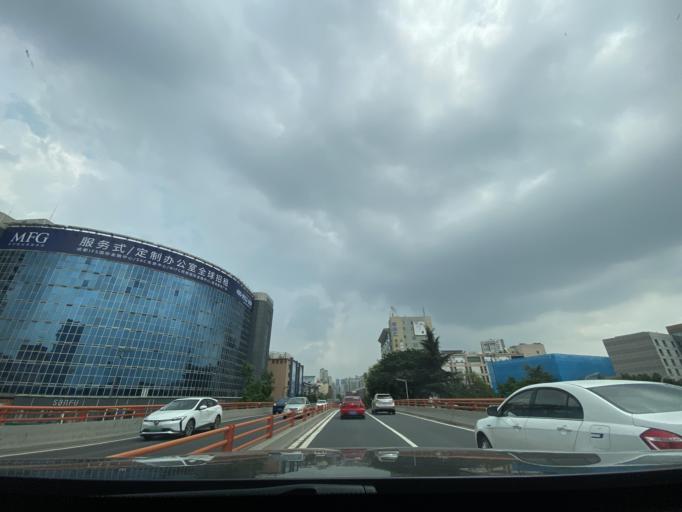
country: CN
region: Sichuan
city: Chengdu
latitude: 30.6360
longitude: 104.0737
